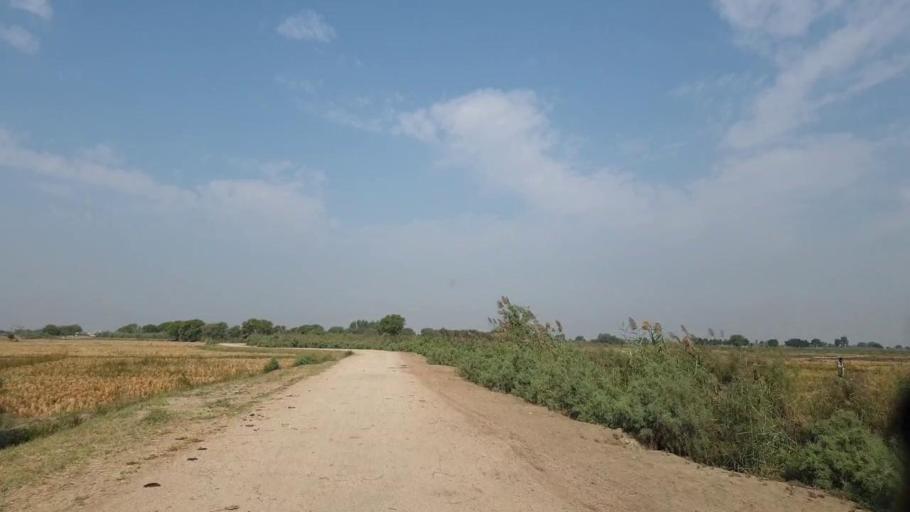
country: PK
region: Sindh
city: Tando Muhammad Khan
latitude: 25.0703
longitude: 68.4348
